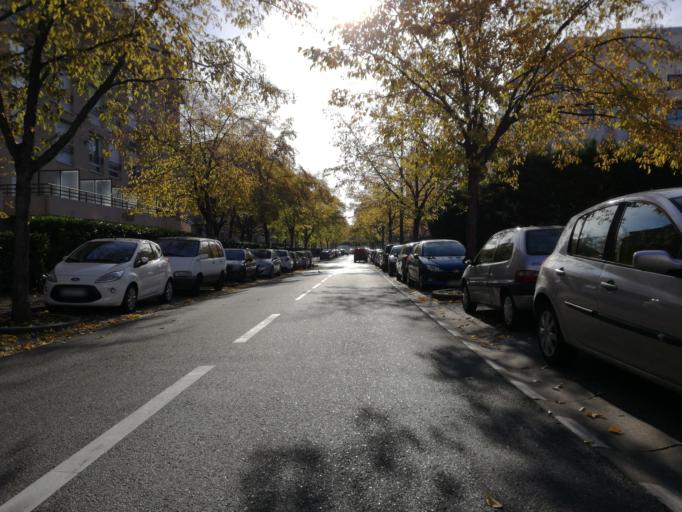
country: FR
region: Rhone-Alpes
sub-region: Departement du Rhone
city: Villeurbanne
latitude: 45.7395
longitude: 4.8760
